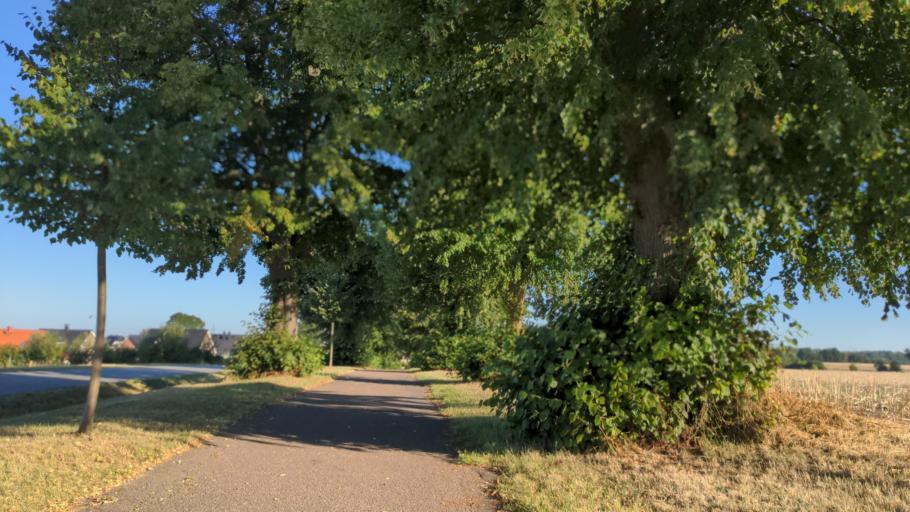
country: DE
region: Mecklenburg-Vorpommern
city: Dassow
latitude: 53.9631
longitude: 10.9686
